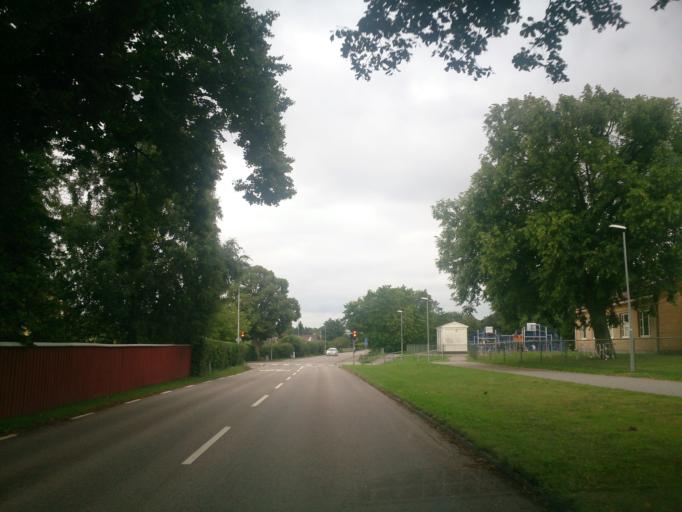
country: SE
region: OEstergoetland
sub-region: Linkopings Kommun
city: Malmslatt
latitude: 58.4175
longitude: 15.5169
